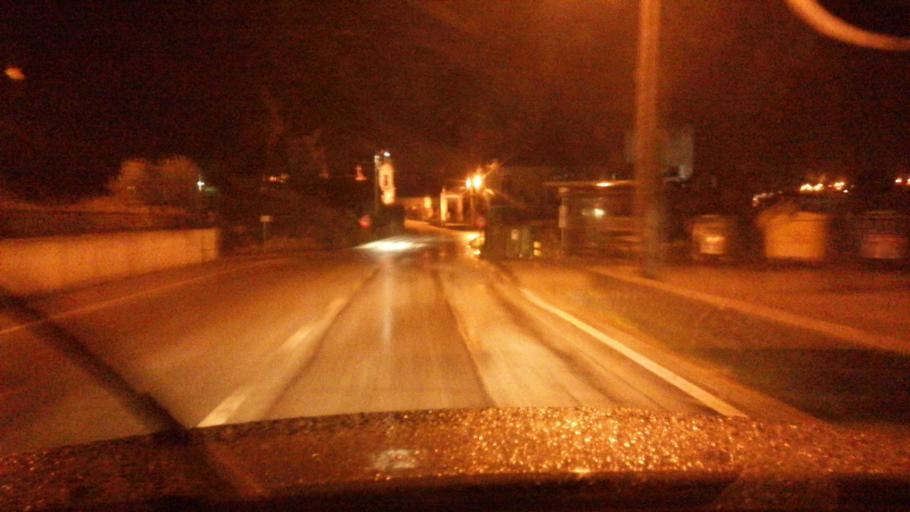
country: PT
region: Viseu
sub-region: Armamar
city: Armamar
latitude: 41.0939
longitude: -7.6853
